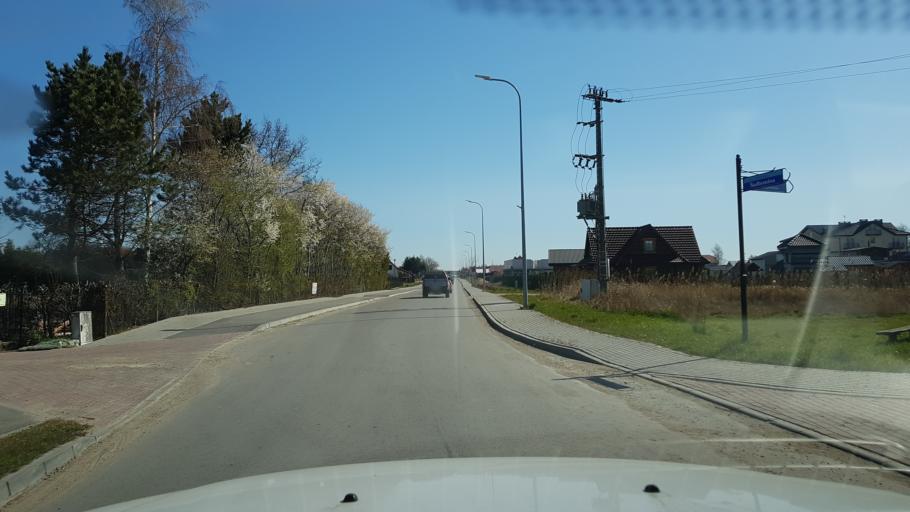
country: PL
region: West Pomeranian Voivodeship
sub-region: Powiat kolobrzeski
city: Ustronie Morskie
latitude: 54.2412
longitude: 15.8754
